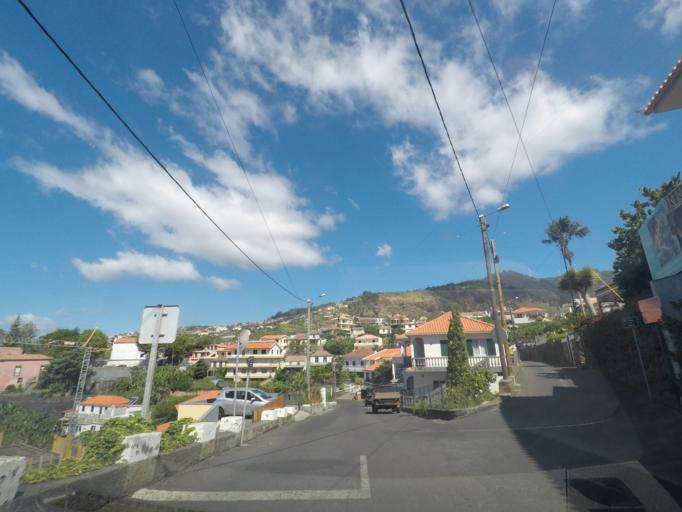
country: PT
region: Madeira
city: Ponta do Sol
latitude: 32.6888
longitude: -17.0900
